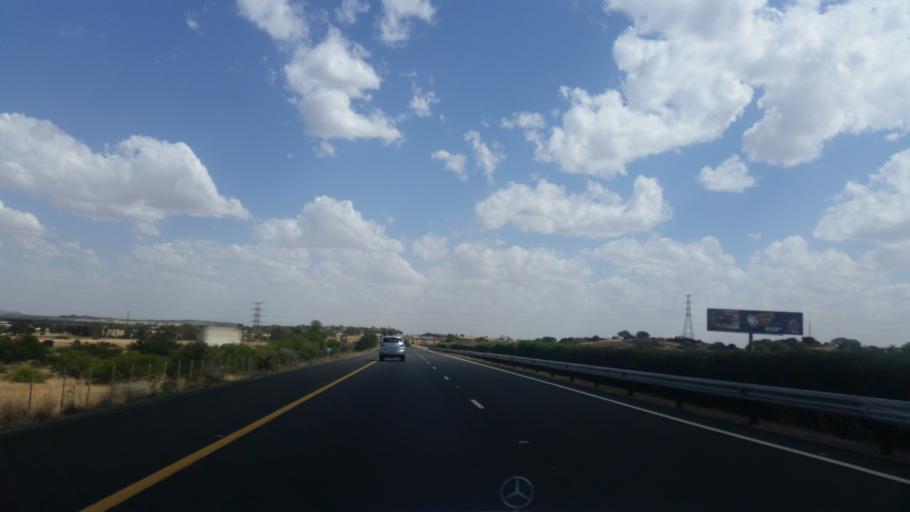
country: ZA
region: Orange Free State
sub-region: Mangaung Metropolitan Municipality
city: Bloemfontein
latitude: -29.0829
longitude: 26.1765
